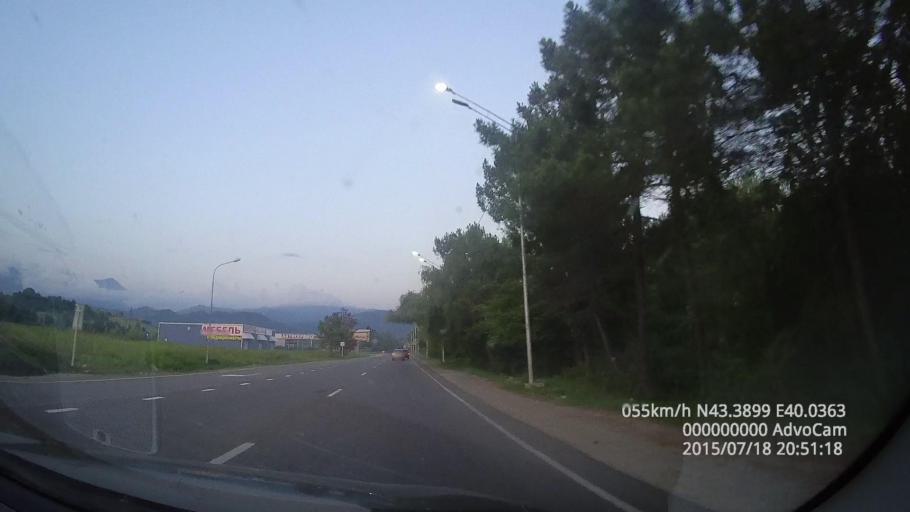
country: GE
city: Gantiadi
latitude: 43.3897
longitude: 40.0377
